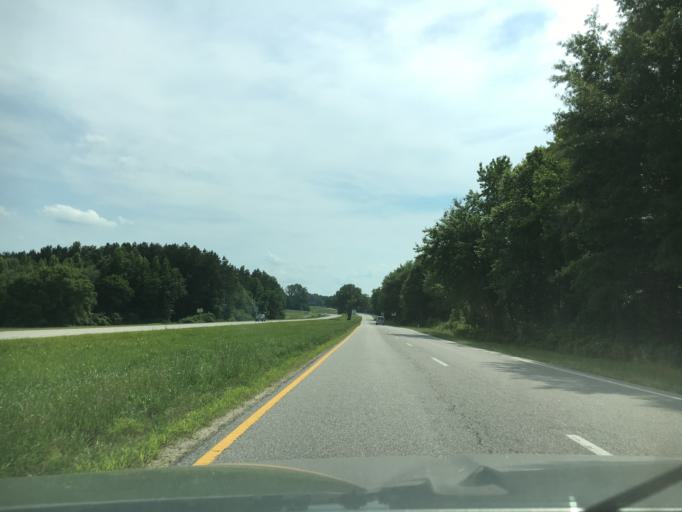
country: US
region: Virginia
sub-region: Nottoway County
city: Crewe
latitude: 37.1957
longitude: -78.1792
